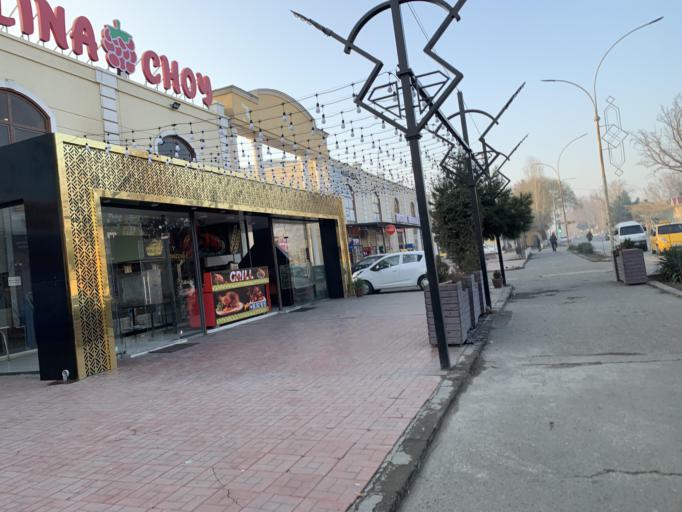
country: UZ
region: Fergana
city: Qo`qon
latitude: 40.5374
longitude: 70.9257
